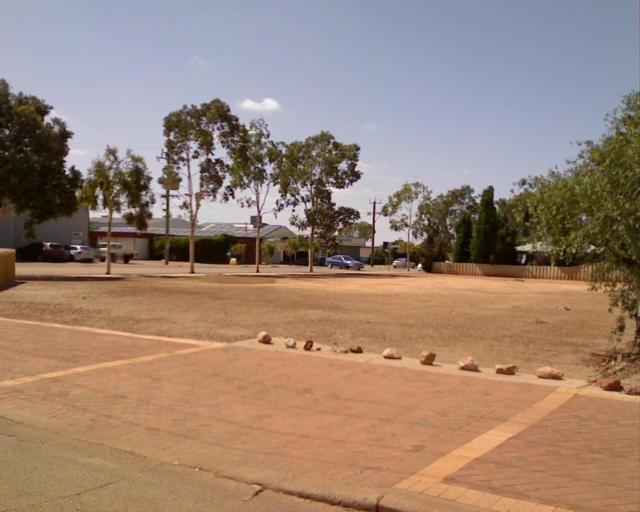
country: AU
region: Western Australia
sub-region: Merredin
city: Merredin
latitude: -30.9145
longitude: 118.2091
